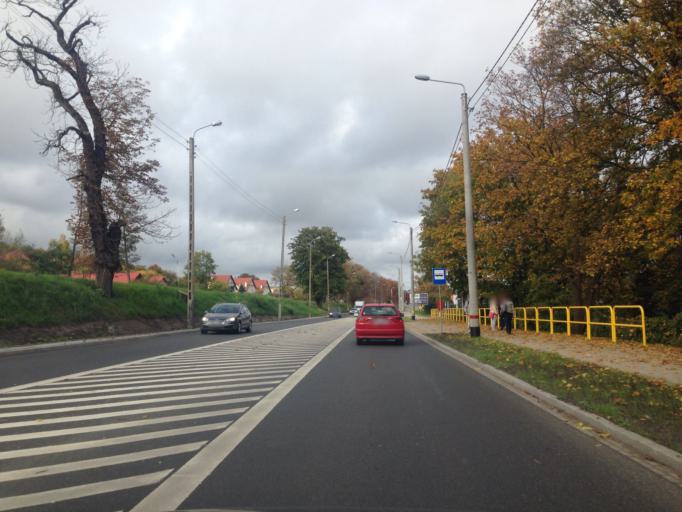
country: PL
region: Pomeranian Voivodeship
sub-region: Powiat gdanski
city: Rotmanka
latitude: 54.3054
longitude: 18.6303
